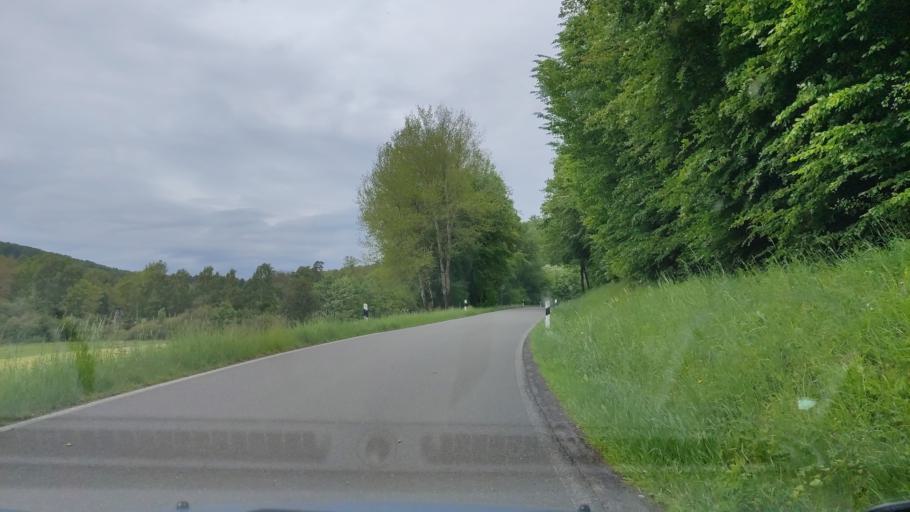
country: DE
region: Lower Saxony
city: Hardegsen
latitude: 51.6993
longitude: 9.7371
